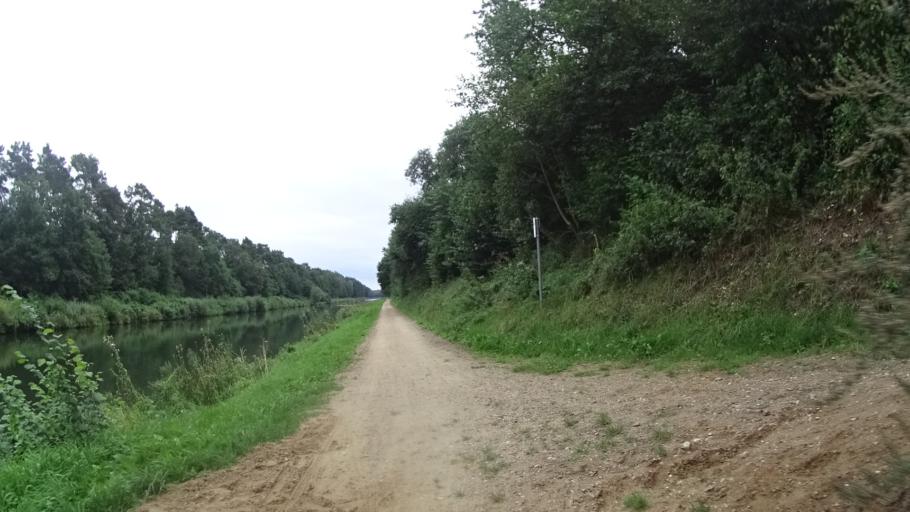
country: DE
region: Schleswig-Holstein
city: Alt Molln
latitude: 53.6018
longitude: 10.6658
